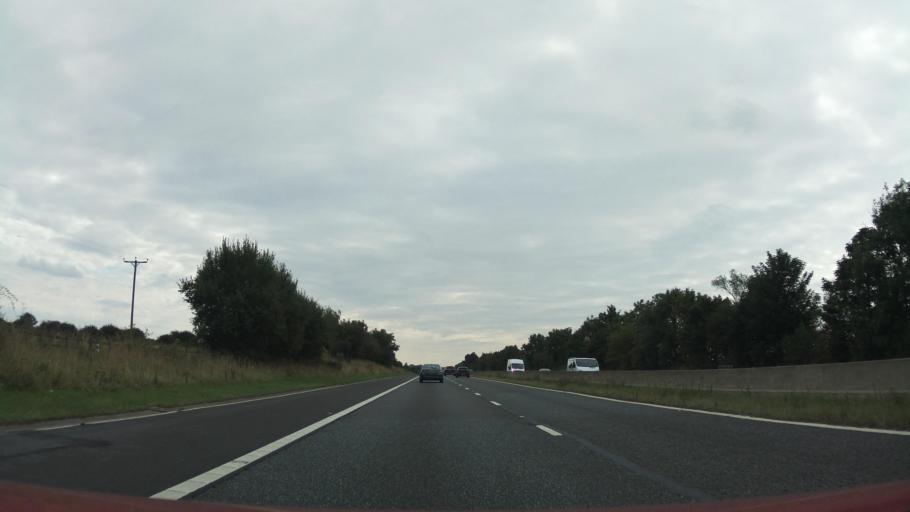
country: GB
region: England
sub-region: County Durham
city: West Rainton
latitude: 54.8343
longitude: -1.5240
